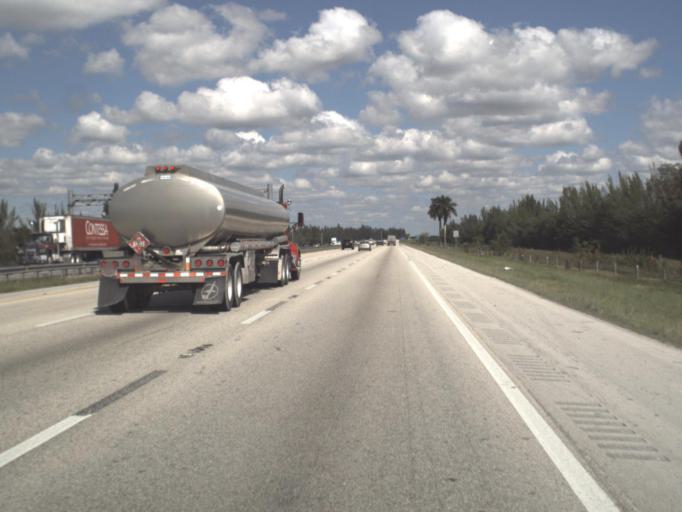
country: US
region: Florida
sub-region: Miami-Dade County
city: Palm Springs North
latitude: 25.9177
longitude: -80.3790
